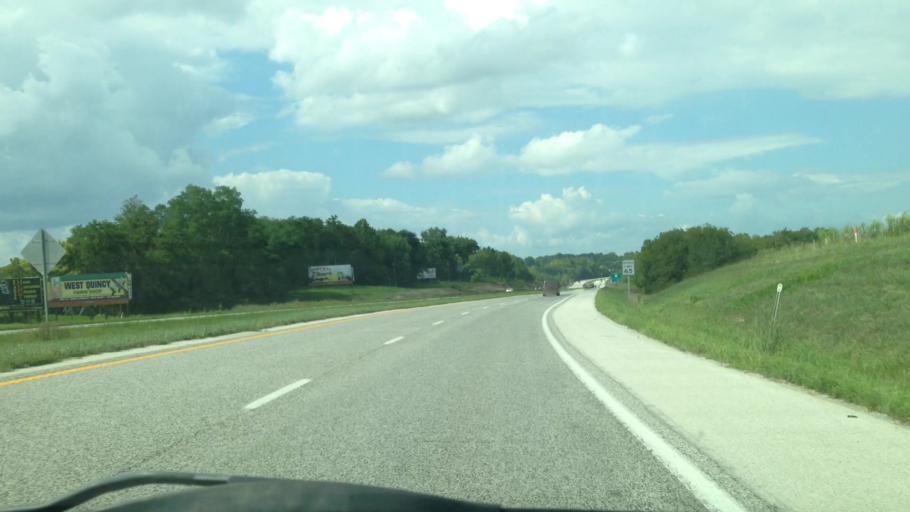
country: US
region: Missouri
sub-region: Marion County
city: Palmyra
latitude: 39.7493
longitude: -91.5172
